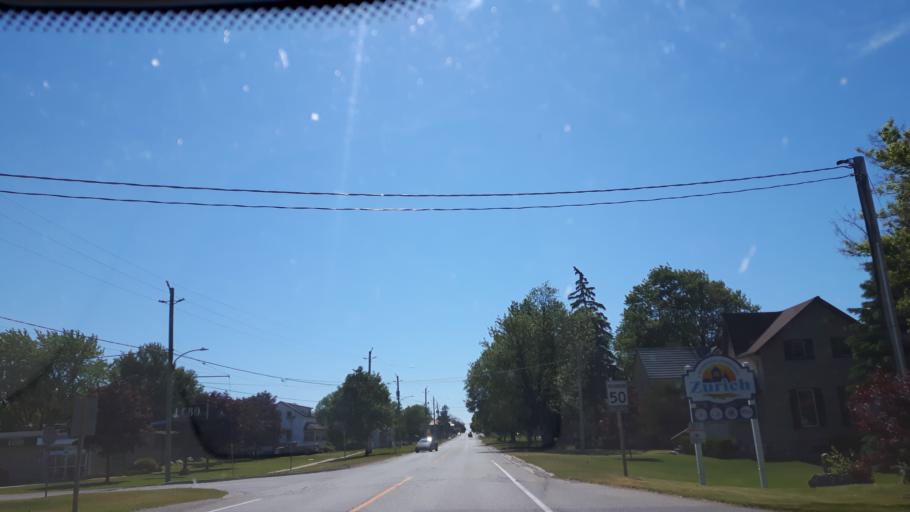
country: CA
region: Ontario
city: Bluewater
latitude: 43.4220
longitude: -81.6181
